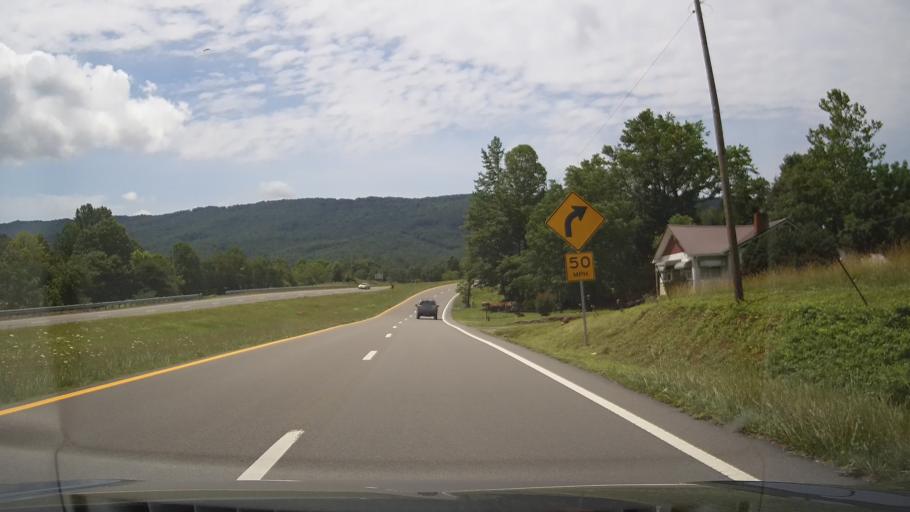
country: US
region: Virginia
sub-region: Lee County
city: Dryden
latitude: 36.7616
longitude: -82.8190
